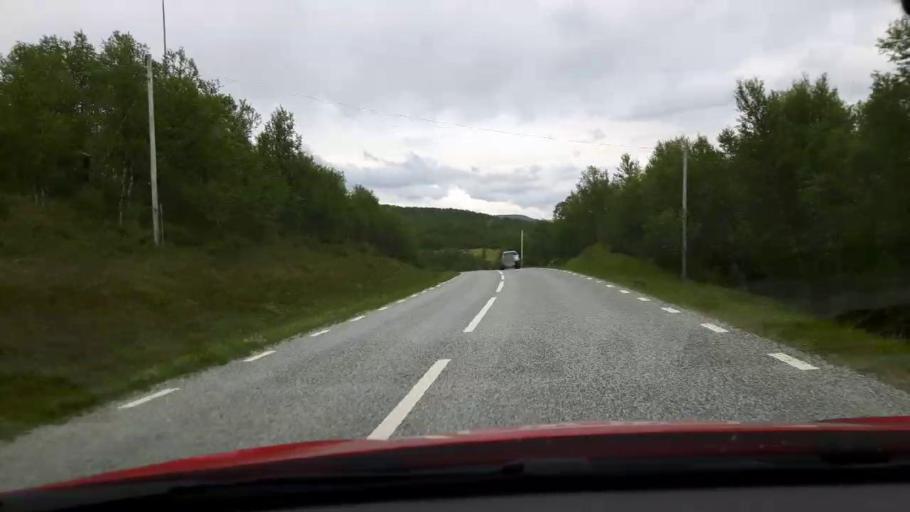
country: NO
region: Sor-Trondelag
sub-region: Tydal
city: Aas
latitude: 62.6014
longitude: 12.1725
